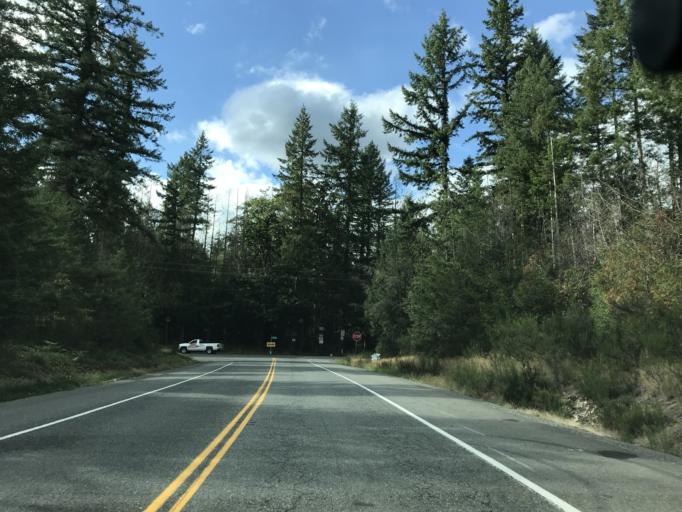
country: US
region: Washington
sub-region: King County
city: Black Diamond
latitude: 47.3009
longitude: -122.0515
